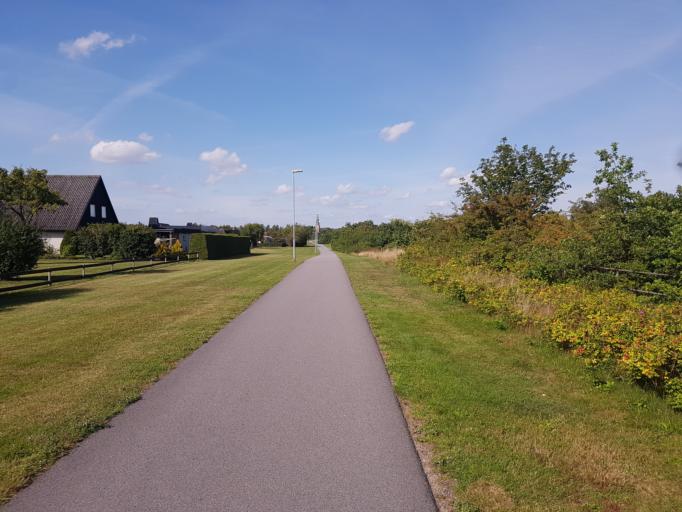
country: SE
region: Skane
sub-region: Sjobo Kommun
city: Sjoebo
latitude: 55.6377
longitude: 13.6994
